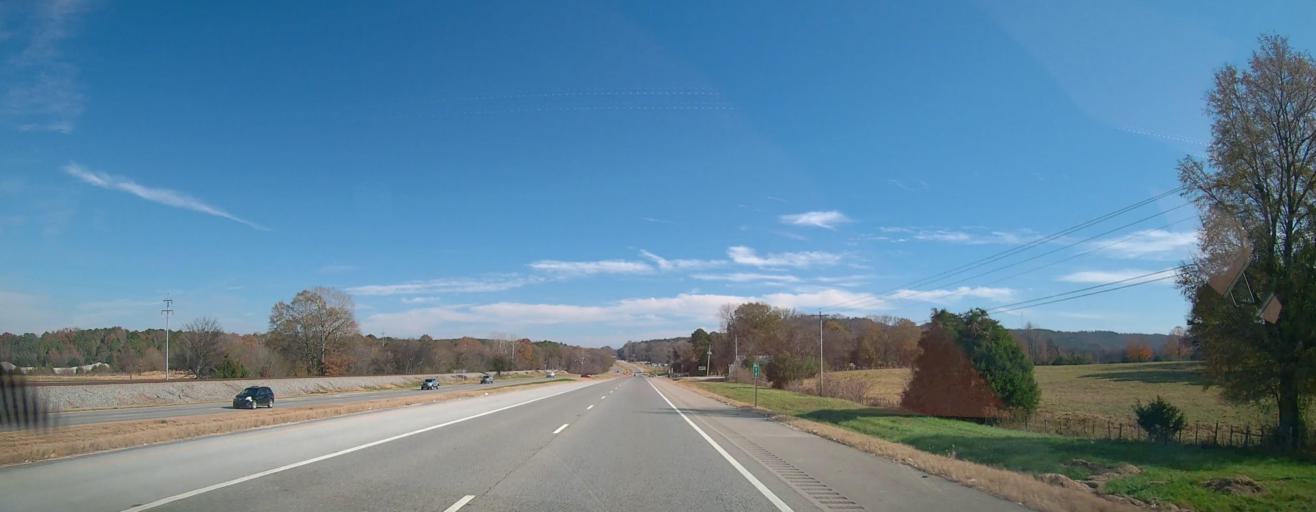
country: US
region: Alabama
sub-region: Colbert County
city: Tuscumbia
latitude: 34.7211
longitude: -87.8073
